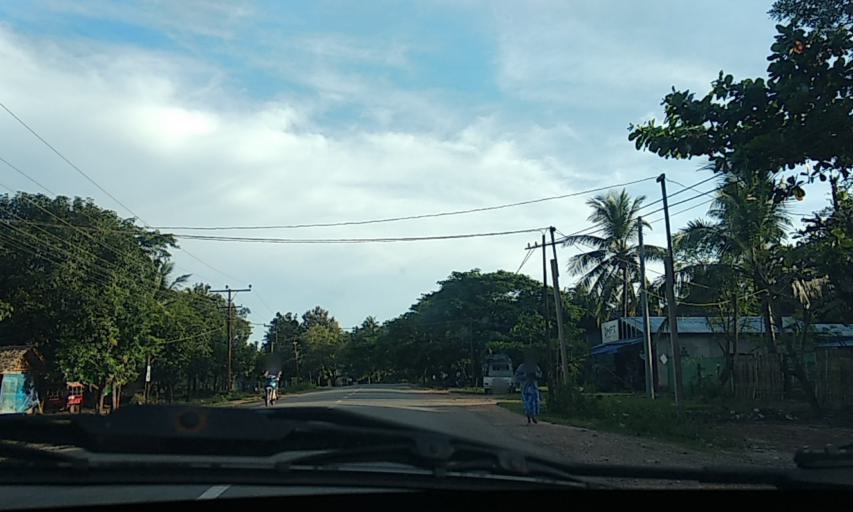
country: MM
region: Mon
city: Mawlamyine
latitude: 16.3998
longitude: 97.7023
